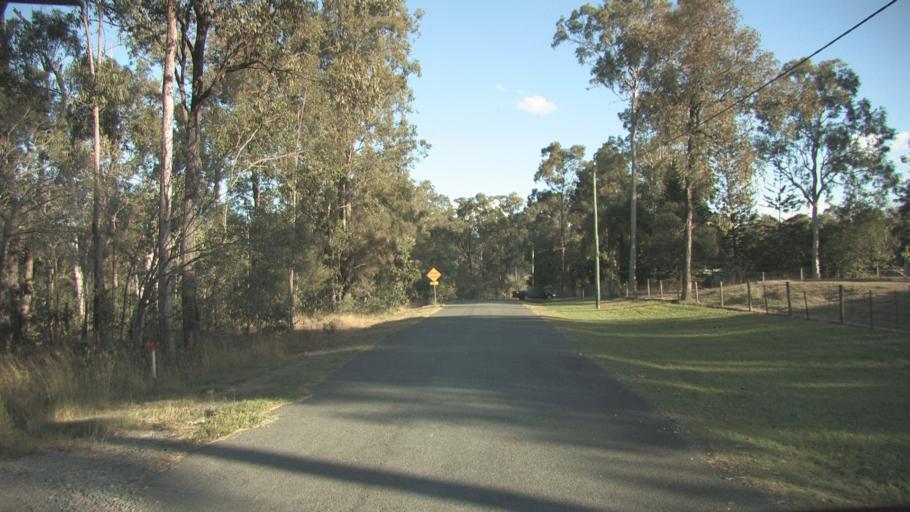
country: AU
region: Queensland
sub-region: Ipswich
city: Springfield Lakes
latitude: -27.6970
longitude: 152.9369
